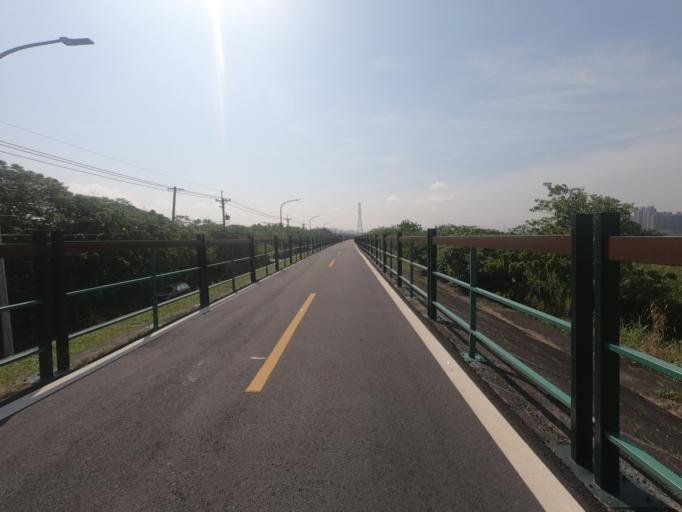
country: TW
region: Taipei
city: Taipei
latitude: 25.1021
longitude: 121.4850
